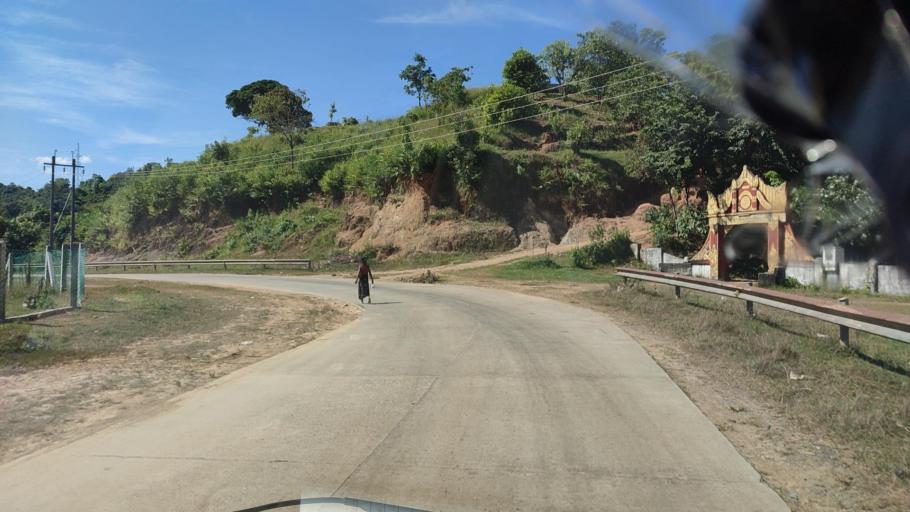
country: MM
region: Rakhine
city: Sittwe
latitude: 20.2260
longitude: 93.4076
